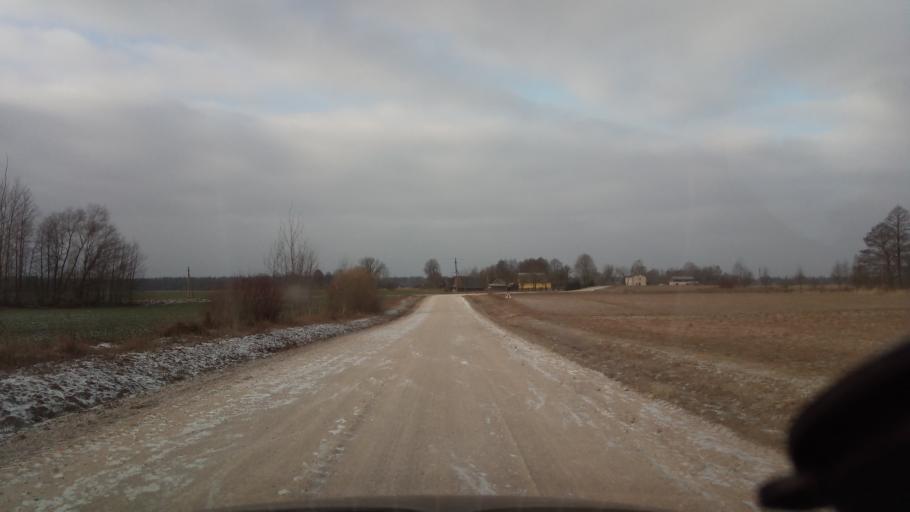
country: LT
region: Alytaus apskritis
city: Varena
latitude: 54.1235
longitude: 24.6641
